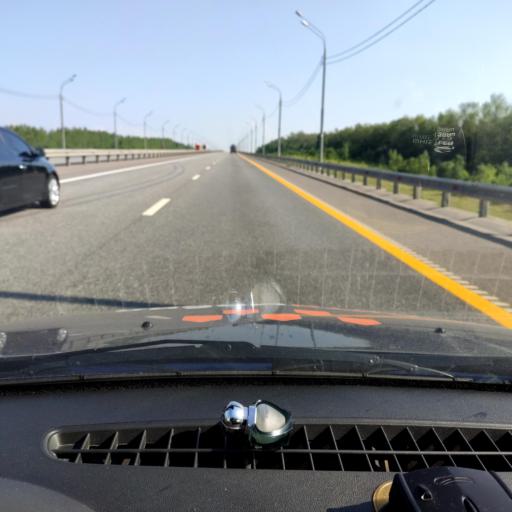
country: RU
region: Lipetsk
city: Khlevnoye
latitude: 52.2793
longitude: 39.0537
